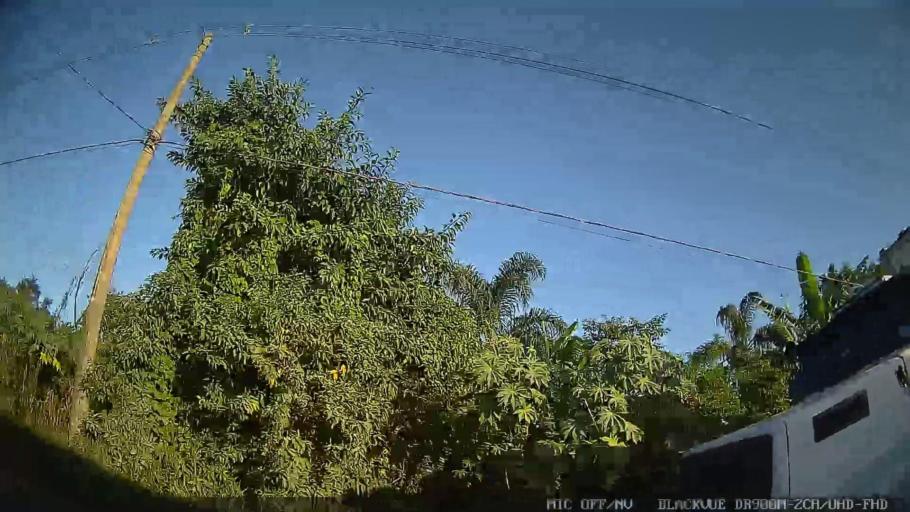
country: BR
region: Sao Paulo
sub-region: Guaruja
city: Guaruja
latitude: -23.9715
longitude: -46.2624
